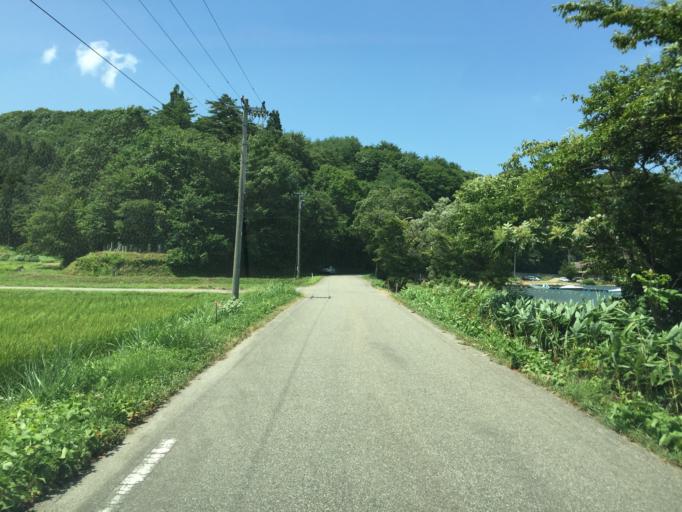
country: JP
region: Fukushima
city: Inawashiro
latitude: 37.4774
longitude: 140.0316
